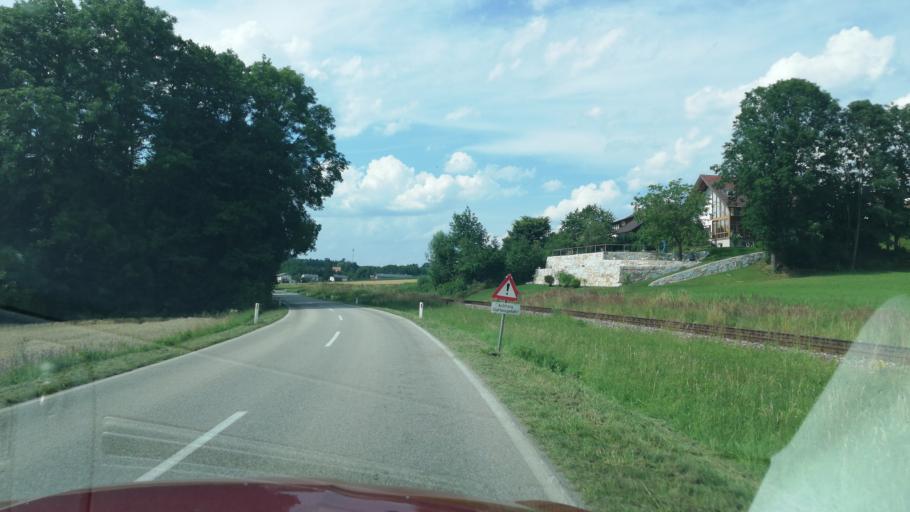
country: AT
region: Upper Austria
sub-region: Politischer Bezirk Vocklabruck
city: Puhret
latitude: 48.0308
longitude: 13.7040
